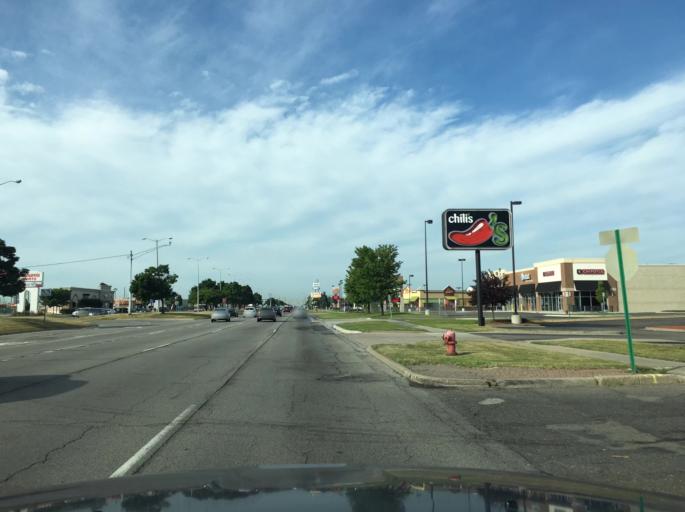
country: US
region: Michigan
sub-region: Macomb County
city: Fraser
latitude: 42.5365
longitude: -82.9114
